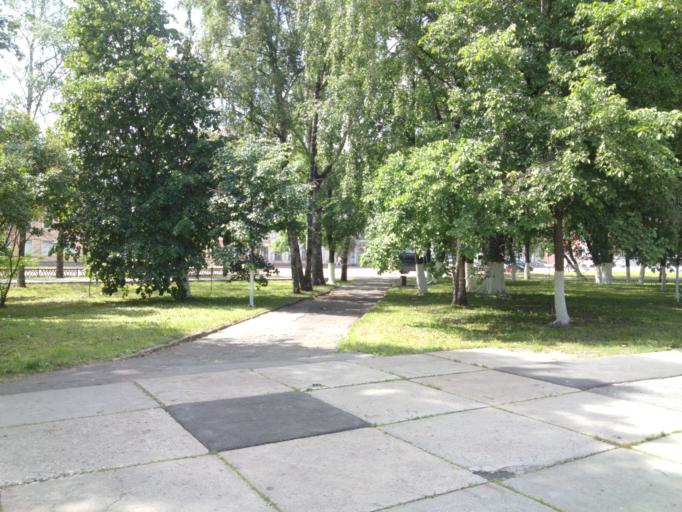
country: RU
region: Vologda
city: Vologda
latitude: 59.2182
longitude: 39.8947
